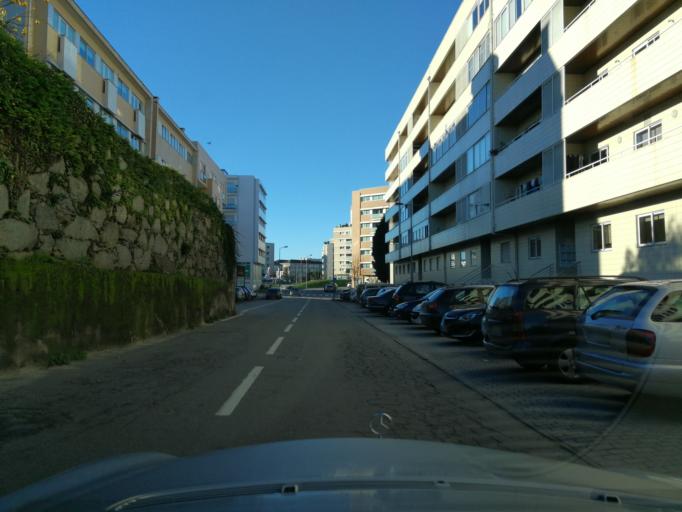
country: PT
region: Braga
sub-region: Braga
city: Braga
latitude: 41.5610
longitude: -8.4136
